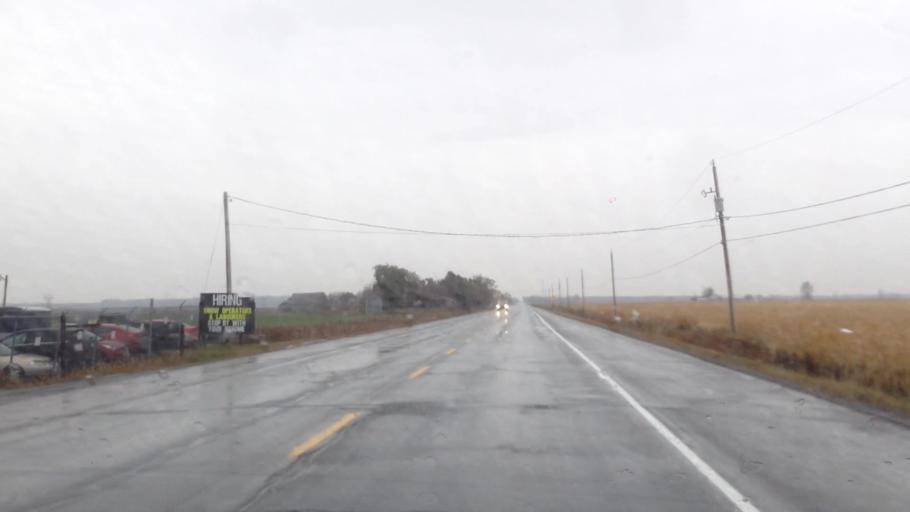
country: CA
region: Ontario
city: Clarence-Rockland
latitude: 45.4623
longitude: -75.4306
